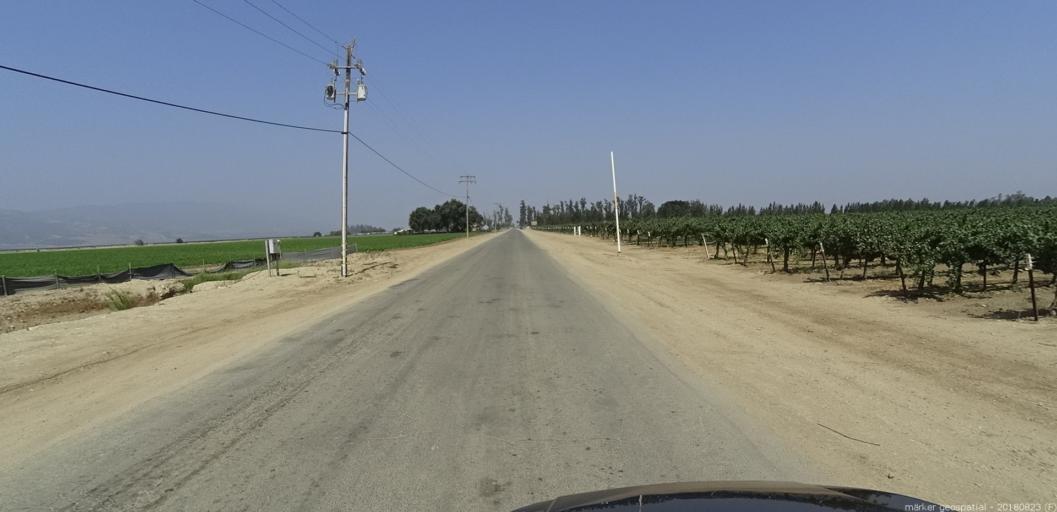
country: US
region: California
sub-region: Monterey County
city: Greenfield
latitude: 36.3054
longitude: -121.2634
